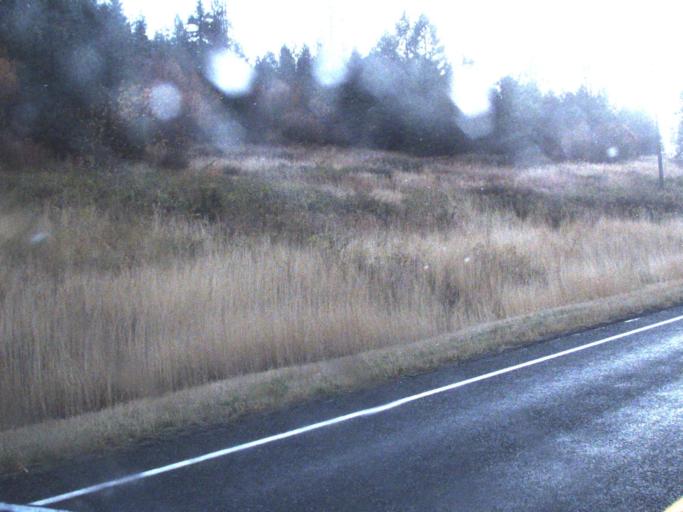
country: US
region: Washington
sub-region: Stevens County
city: Kettle Falls
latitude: 48.4677
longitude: -118.1768
